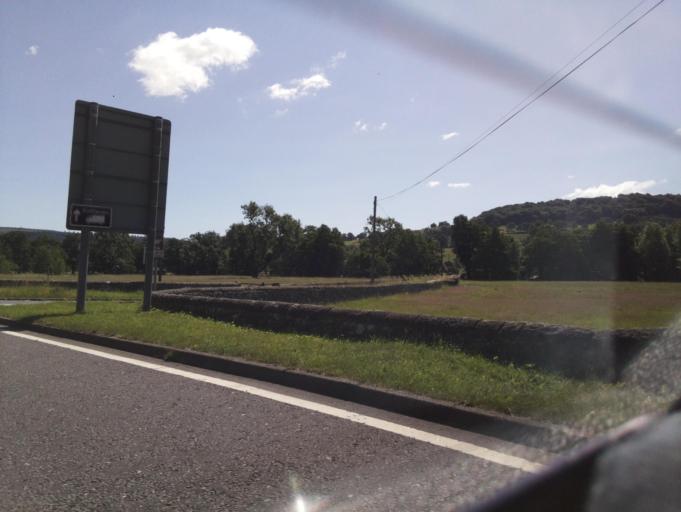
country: GB
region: England
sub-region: Derbyshire
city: Bakewell
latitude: 53.1891
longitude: -1.6419
